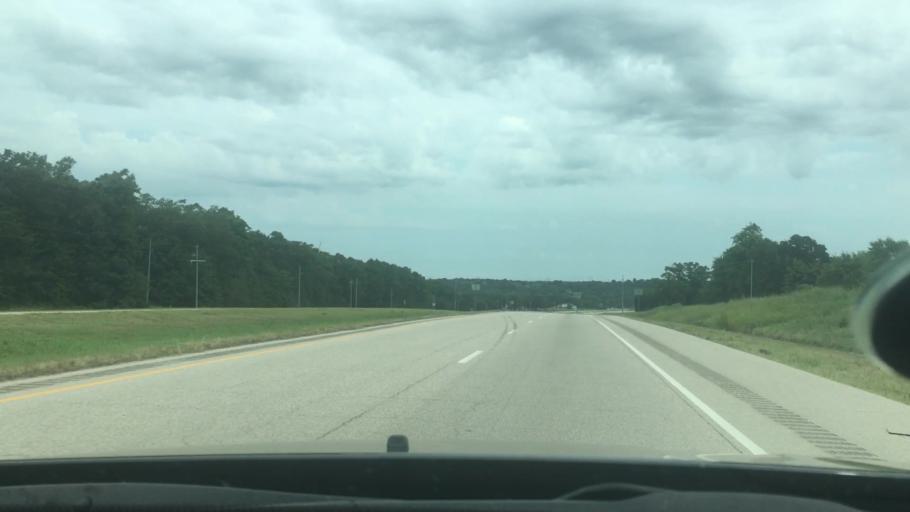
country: US
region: Oklahoma
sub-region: Pontotoc County
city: Byng
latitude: 34.9175
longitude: -96.6814
